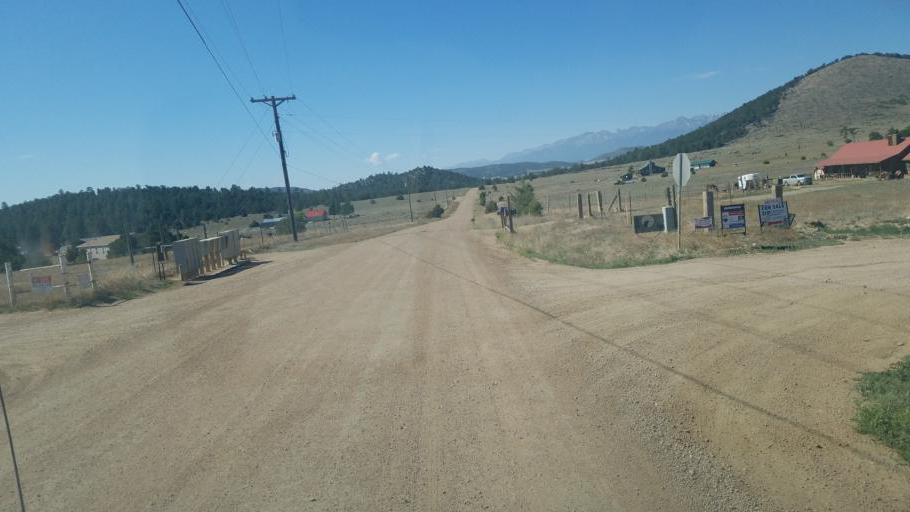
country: US
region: Colorado
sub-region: Custer County
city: Westcliffe
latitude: 38.3103
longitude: -105.4864
